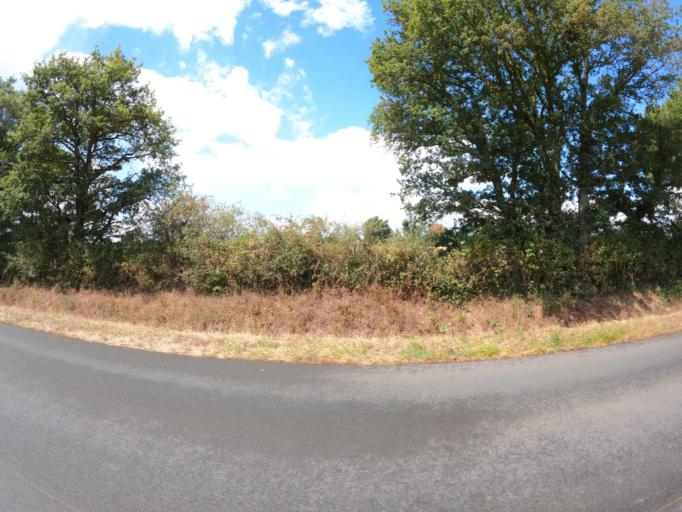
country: FR
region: Pays de la Loire
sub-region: Departement de Maine-et-Loire
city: Feneu
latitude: 47.5903
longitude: -0.5898
